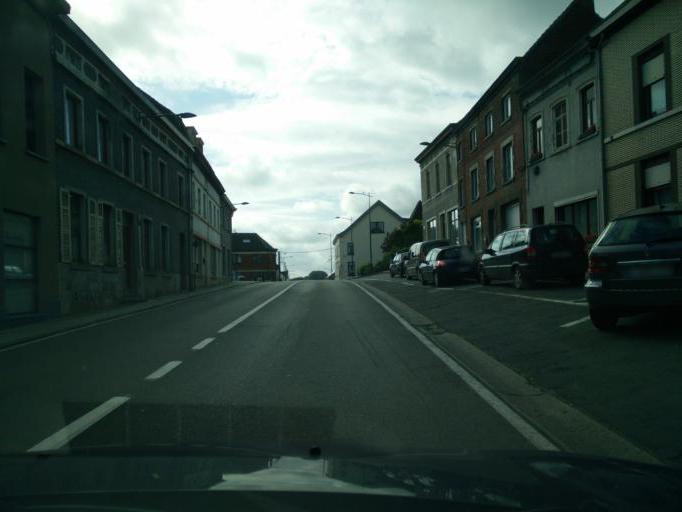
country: BE
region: Wallonia
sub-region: Province du Hainaut
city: Flobecq
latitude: 50.7365
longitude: 3.7390
